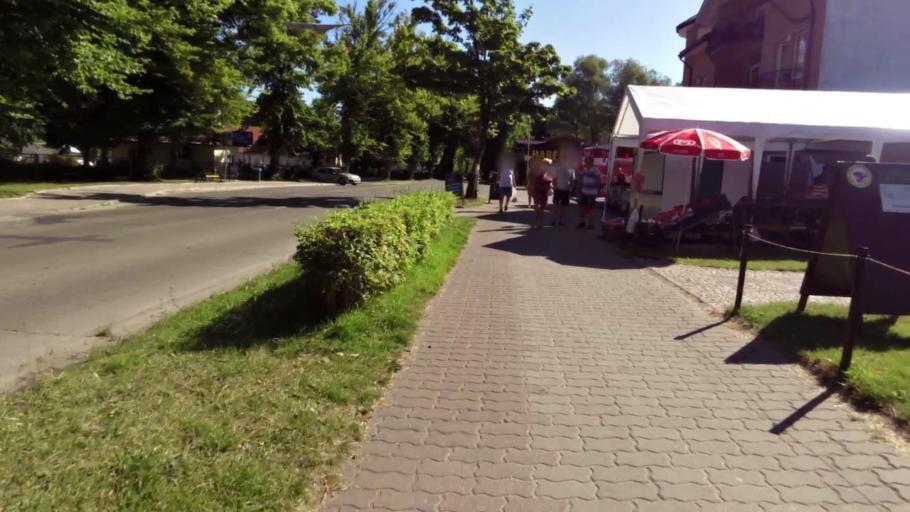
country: PL
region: West Pomeranian Voivodeship
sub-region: Powiat koszalinski
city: Mielno
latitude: 54.2640
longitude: 16.0766
